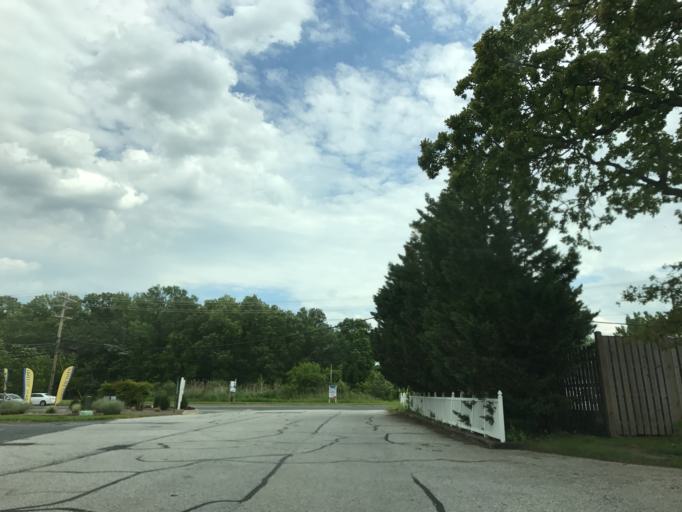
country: US
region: Maryland
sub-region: Baltimore County
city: Bowleys Quarters
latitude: 39.3371
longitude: -76.4088
